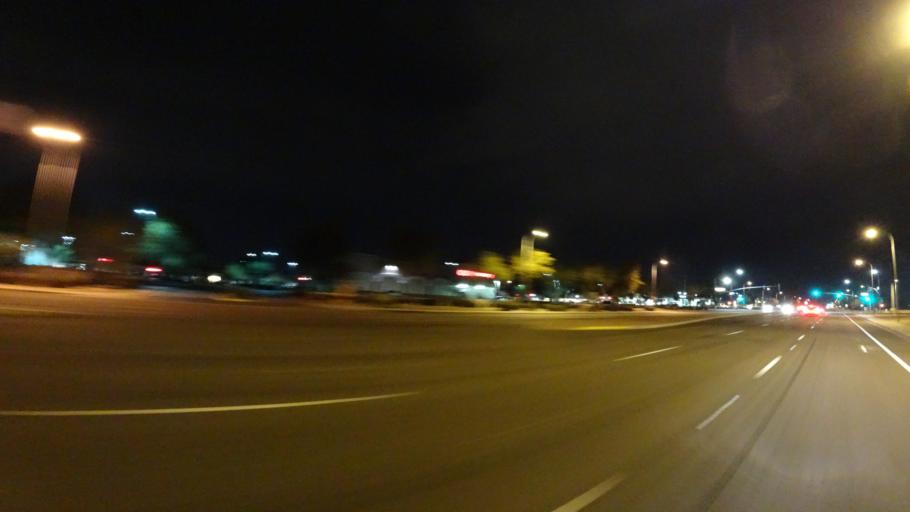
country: US
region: Arizona
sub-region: Maricopa County
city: Chandler
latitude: 33.2916
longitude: -111.8258
